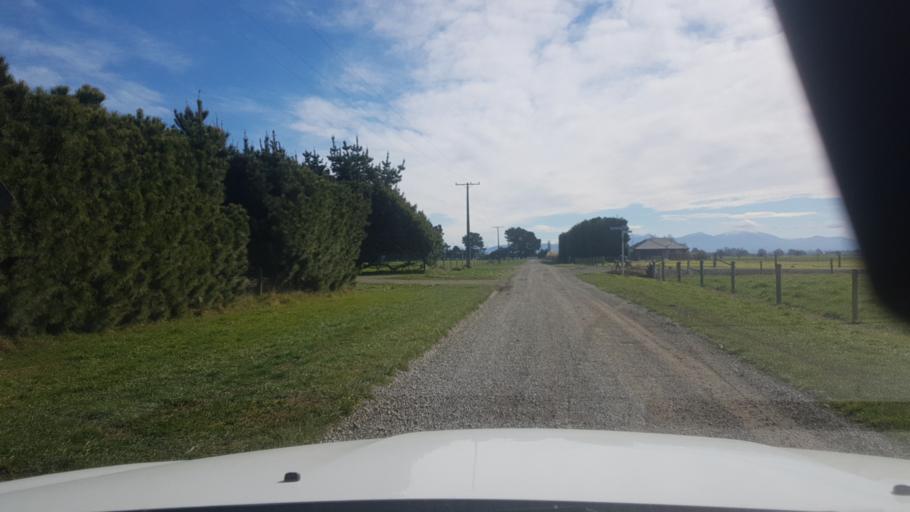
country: NZ
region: Canterbury
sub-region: Timaru District
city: Timaru
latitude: -44.2481
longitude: 171.3824
